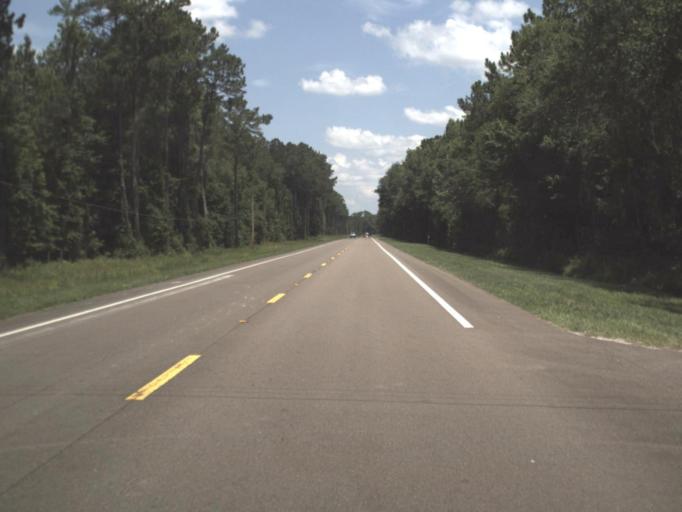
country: US
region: Florida
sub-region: Alachua County
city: Alachua
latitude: 29.7658
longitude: -82.3638
